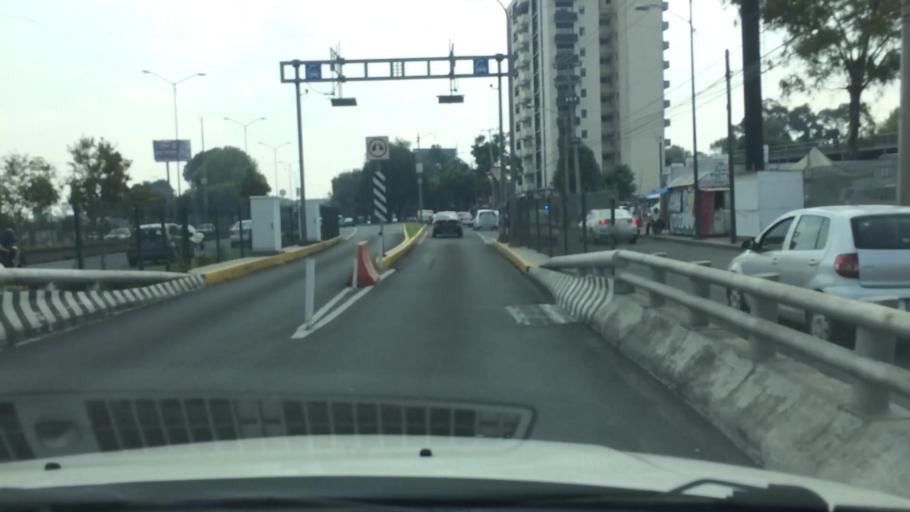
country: MX
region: Mexico City
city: Tlalpan
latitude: 19.2859
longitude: -99.1483
